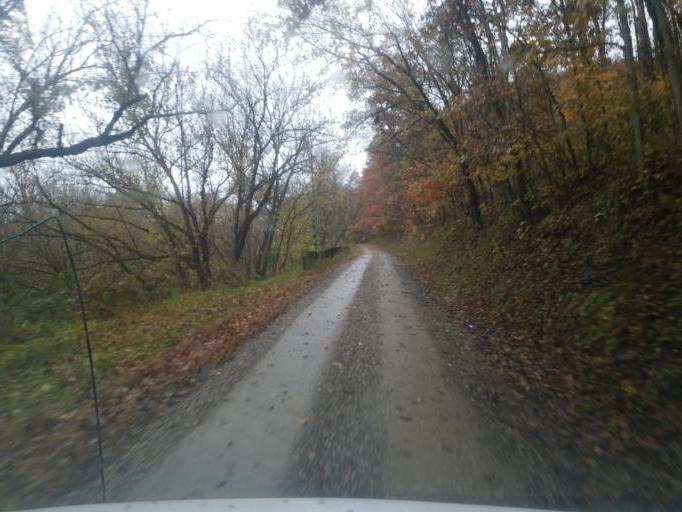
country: US
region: Ohio
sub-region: Washington County
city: Beverly
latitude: 39.4593
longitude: -81.7768
